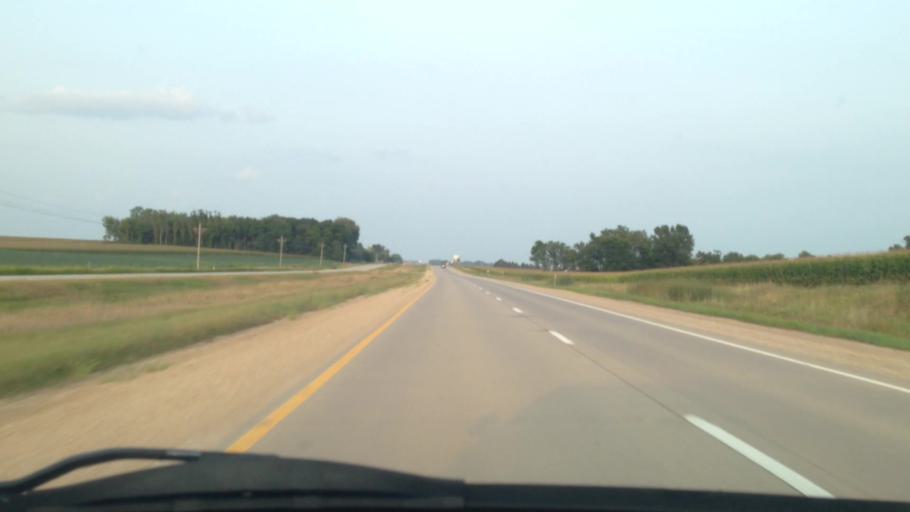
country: US
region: Iowa
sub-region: Benton County
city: Atkins
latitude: 41.9632
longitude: -91.8862
